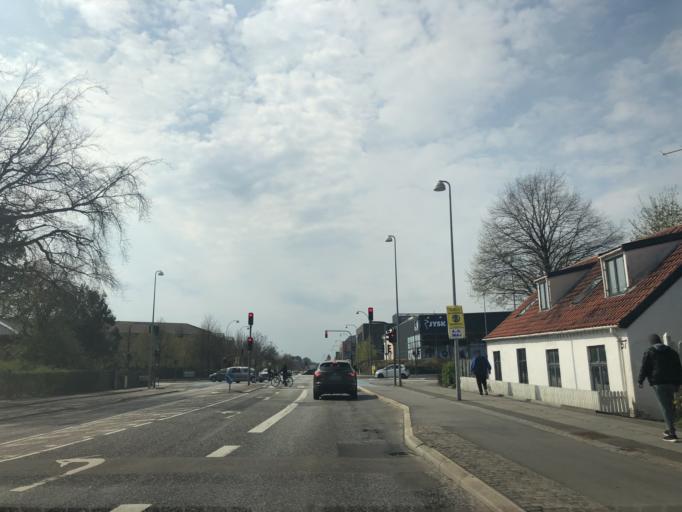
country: DK
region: Zealand
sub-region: Roskilde Kommune
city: Roskilde
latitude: 55.6413
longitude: 12.1050
